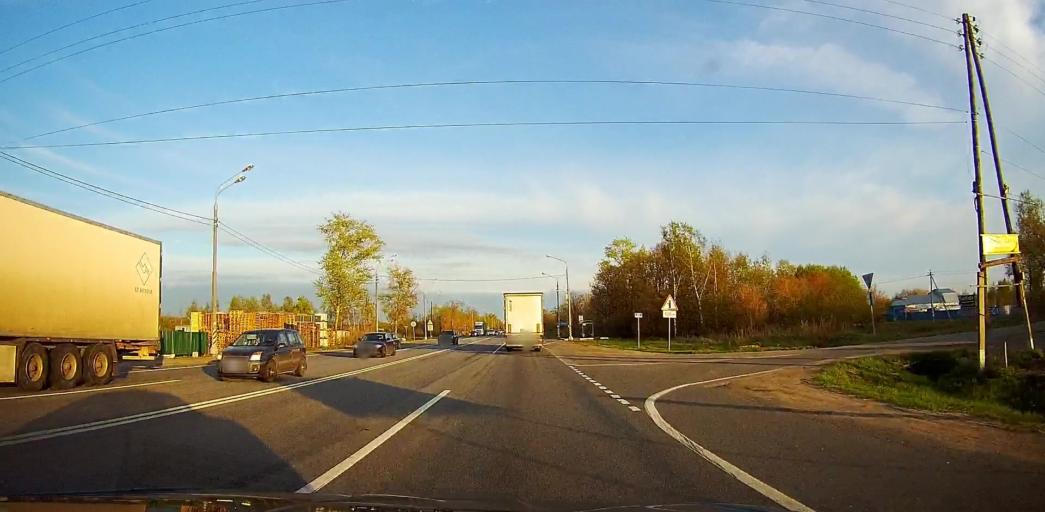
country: RU
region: Moskovskaya
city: Troitskoye
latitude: 55.2625
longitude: 38.5086
